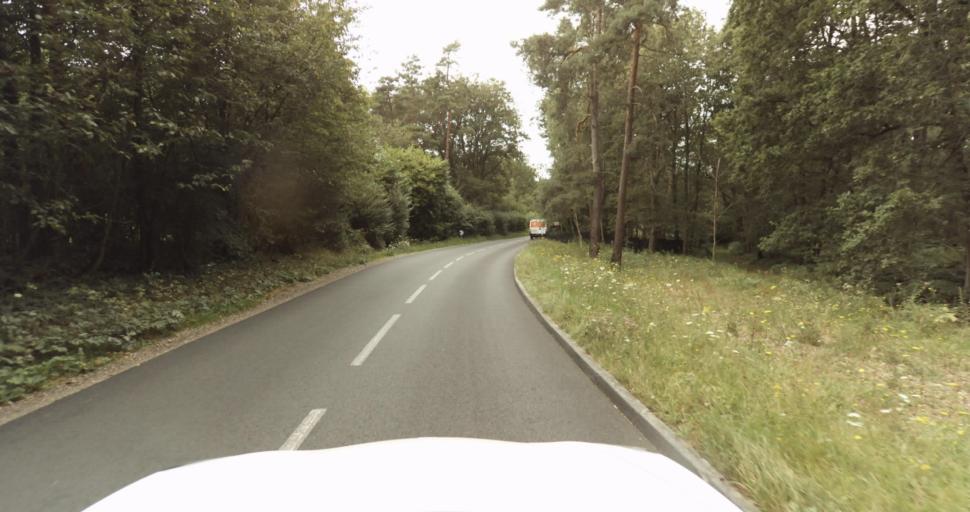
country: FR
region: Haute-Normandie
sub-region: Departement de l'Eure
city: Saint-Sebastien-de-Morsent
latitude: 48.9895
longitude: 1.0558
